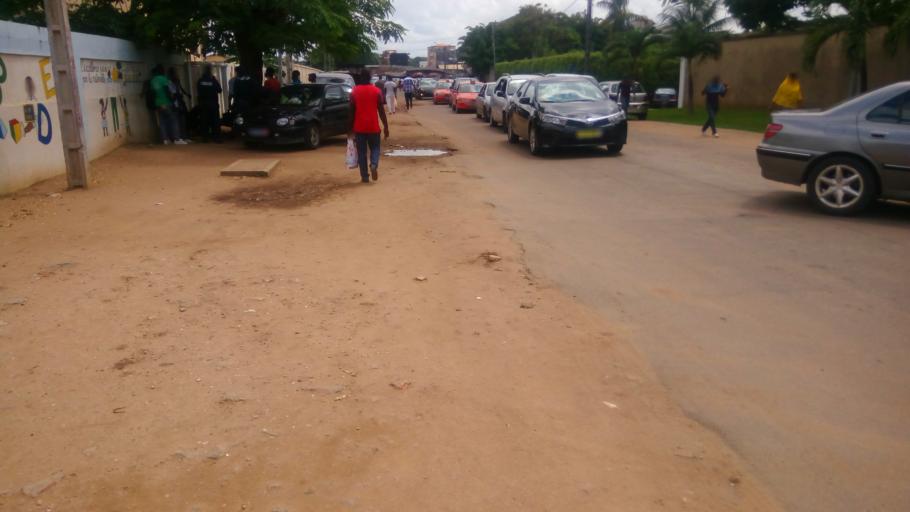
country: CI
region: Lagunes
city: Abidjan
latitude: 5.3383
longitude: -4.0224
